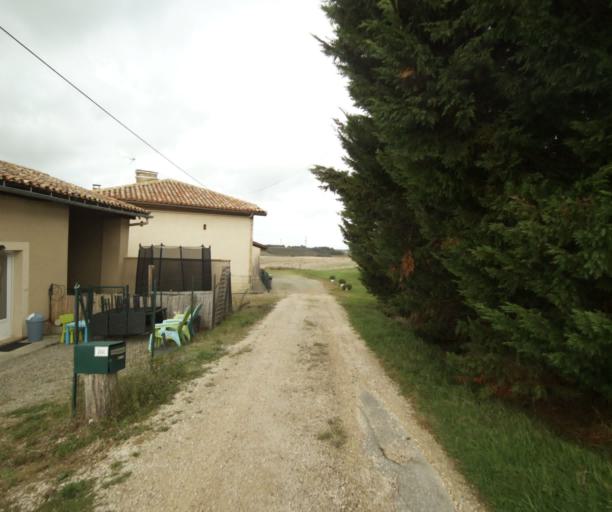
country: FR
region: Midi-Pyrenees
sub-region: Departement du Tarn-et-Garonne
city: Beaumont-de-Lomagne
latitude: 43.9030
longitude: 1.0906
